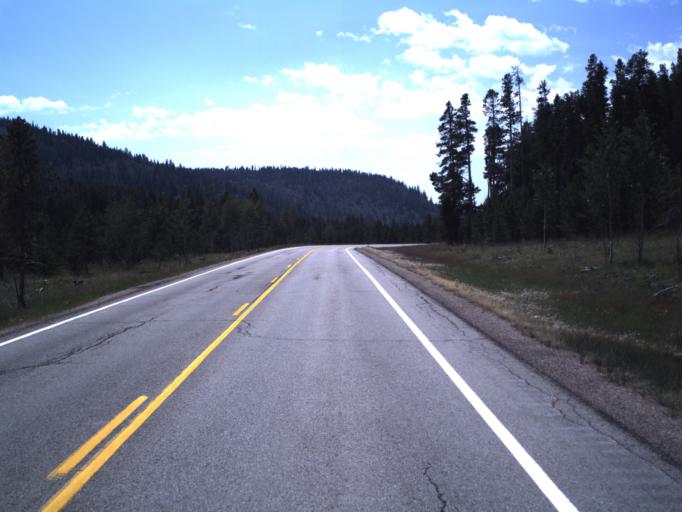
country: US
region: Utah
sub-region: Daggett County
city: Manila
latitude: 40.8272
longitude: -109.4621
